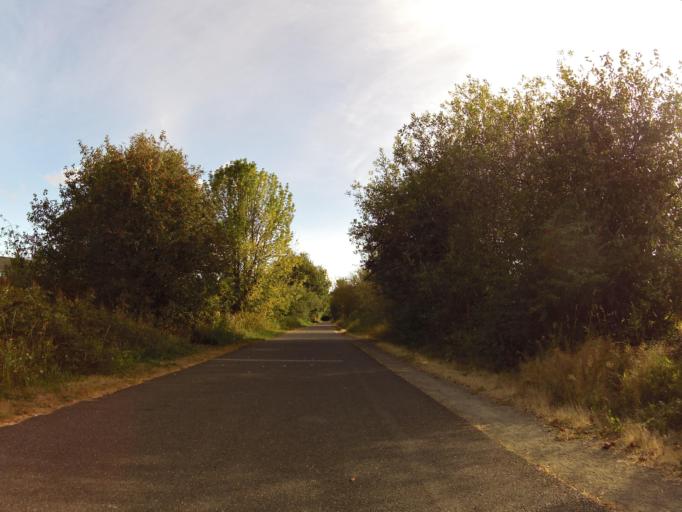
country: US
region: Washington
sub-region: Thurston County
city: Lacey
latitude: 47.0141
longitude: -122.8338
